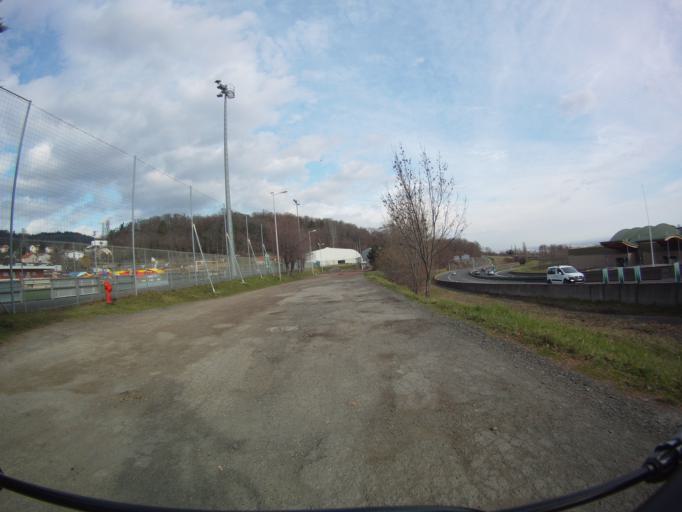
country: FR
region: Auvergne
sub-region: Departement du Puy-de-Dome
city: Ceyrat
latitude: 45.7349
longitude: 3.0675
